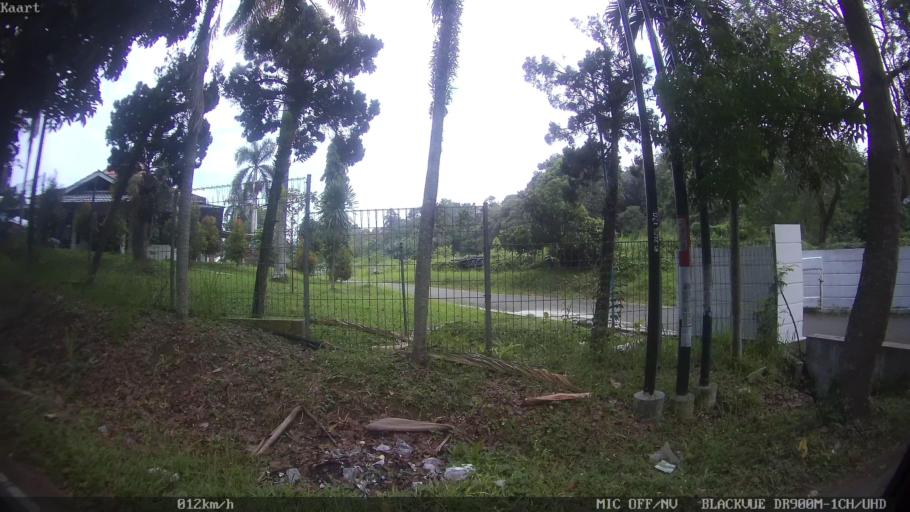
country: ID
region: Lampung
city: Bandarlampung
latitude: -5.4335
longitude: 105.2468
